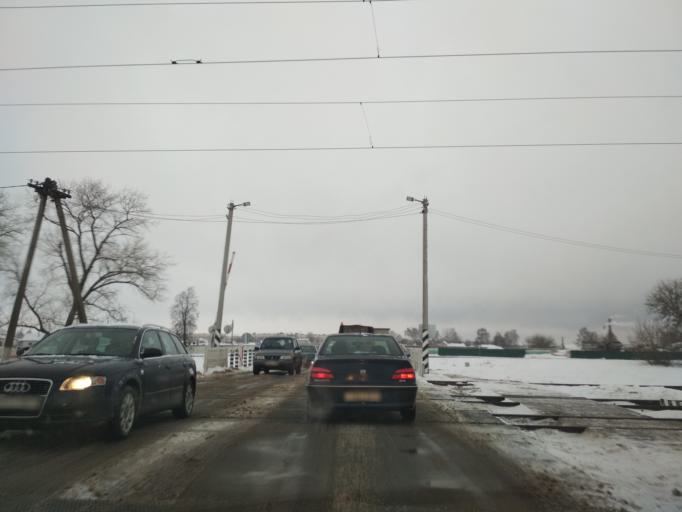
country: BY
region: Minsk
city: Mar''ina Horka
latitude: 53.4989
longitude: 28.1499
